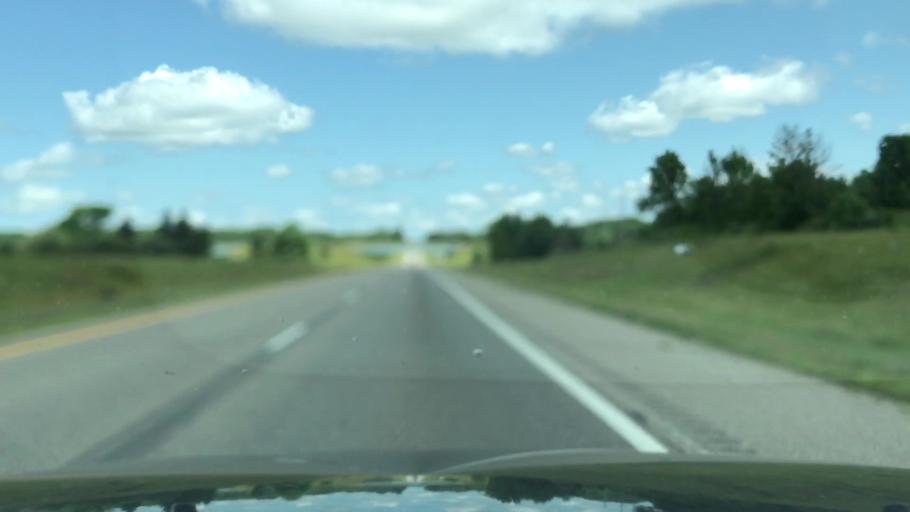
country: US
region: Michigan
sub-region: Mecosta County
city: Big Rapids
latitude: 43.7118
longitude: -85.5295
